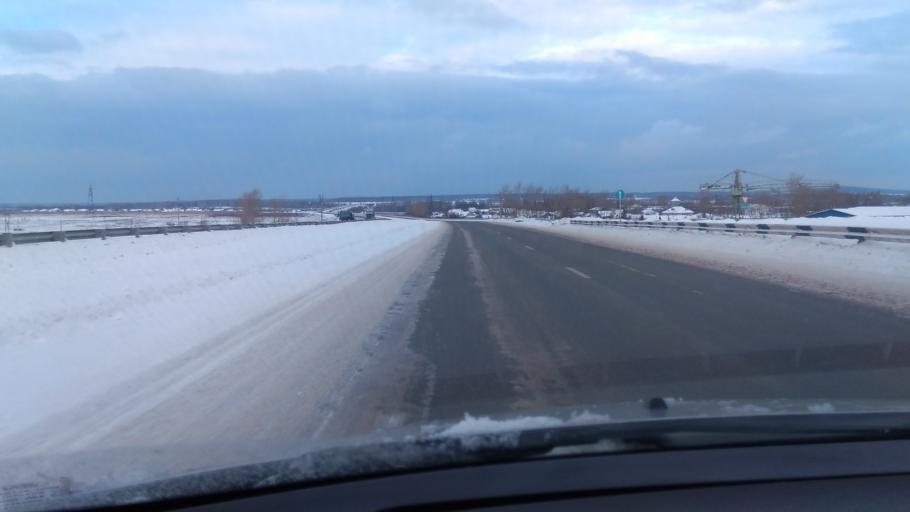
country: RU
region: Sverdlovsk
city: Tsementnyy
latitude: 57.4834
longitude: 60.1801
